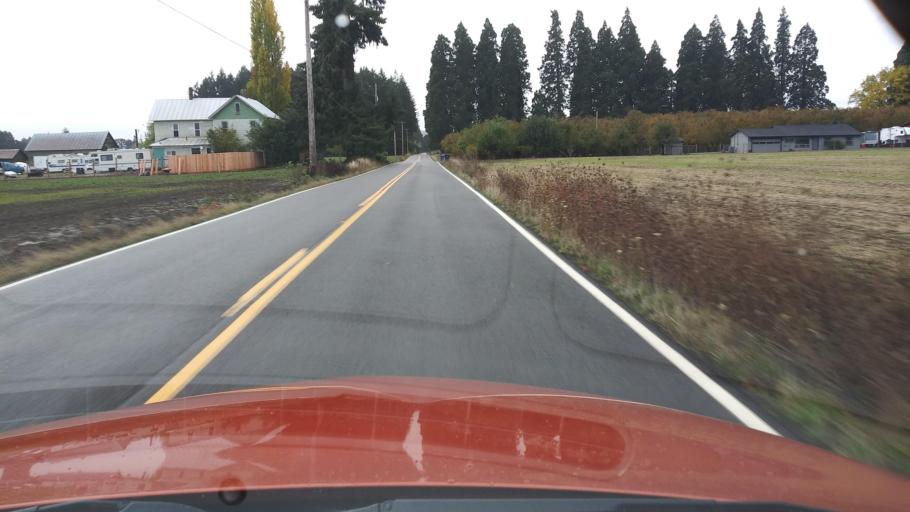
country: US
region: Oregon
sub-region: Washington County
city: Forest Grove
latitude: 45.5400
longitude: -123.0870
